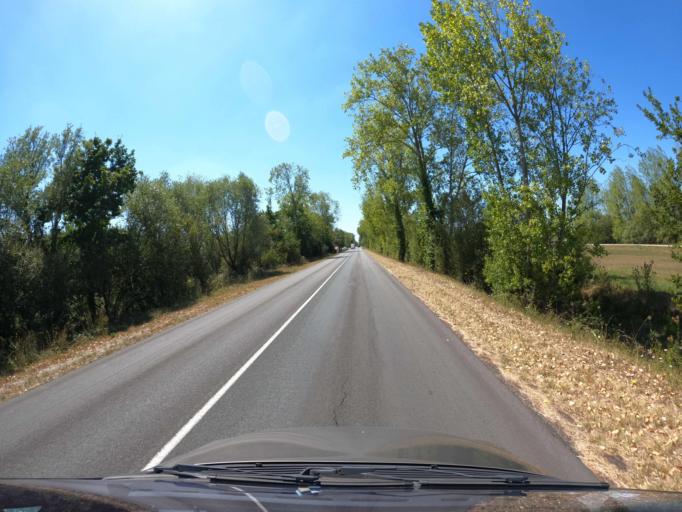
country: FR
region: Pays de la Loire
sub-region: Departement de la Vendee
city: Le Perrier
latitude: 46.8177
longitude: -1.9963
